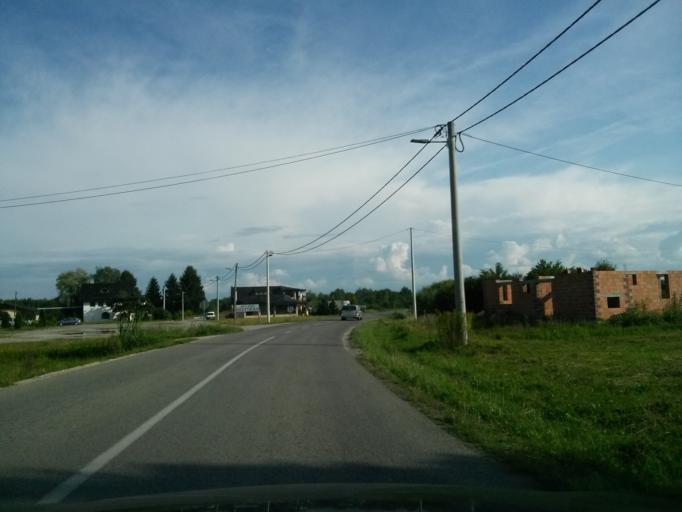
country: HR
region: Grad Zagreb
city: Horvati
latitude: 45.5682
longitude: 15.8636
